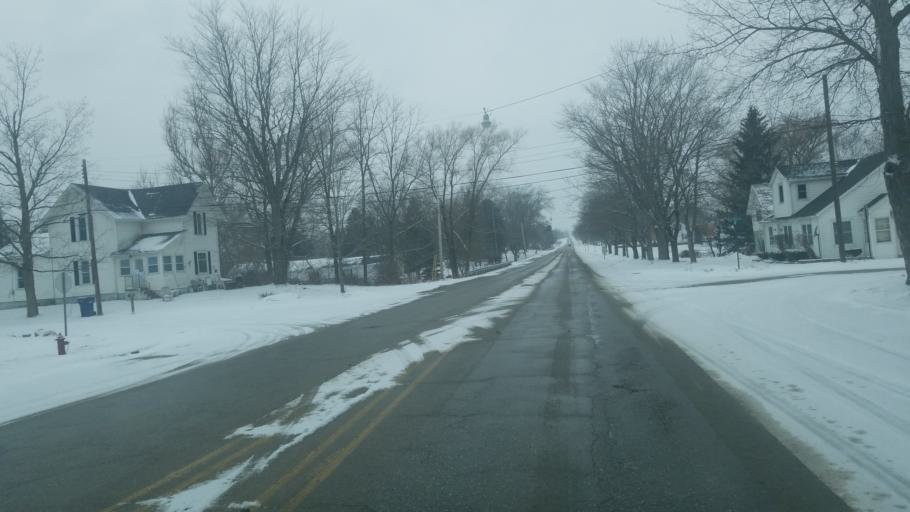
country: US
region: Michigan
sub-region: Osceola County
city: Evart
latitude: 44.1025
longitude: -85.1496
